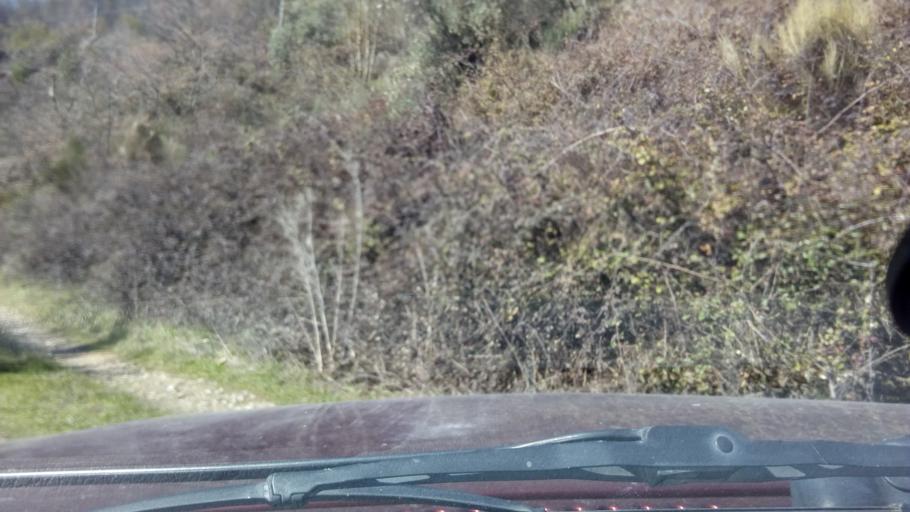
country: PT
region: Guarda
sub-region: Fornos de Algodres
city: Fornos de Algodres
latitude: 40.6159
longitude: -7.5135
